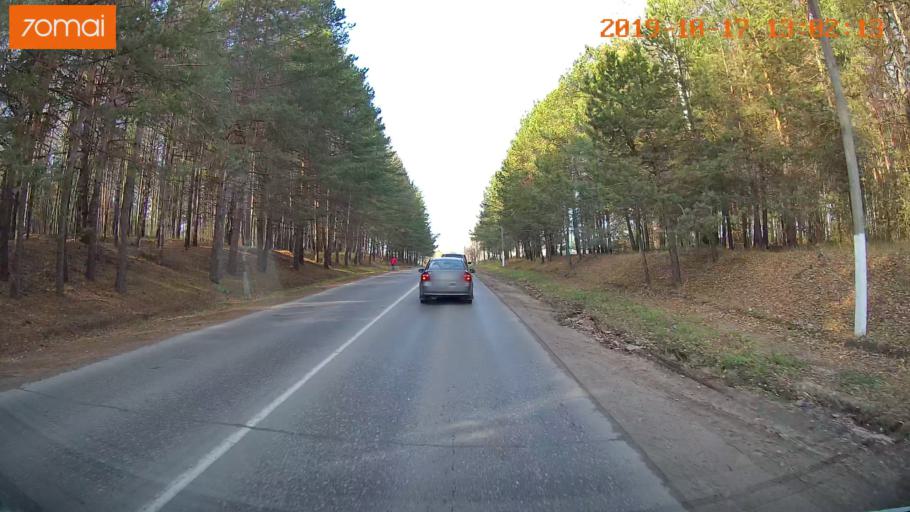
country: RU
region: Rjazan
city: Kasimov
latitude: 54.9490
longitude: 41.3632
